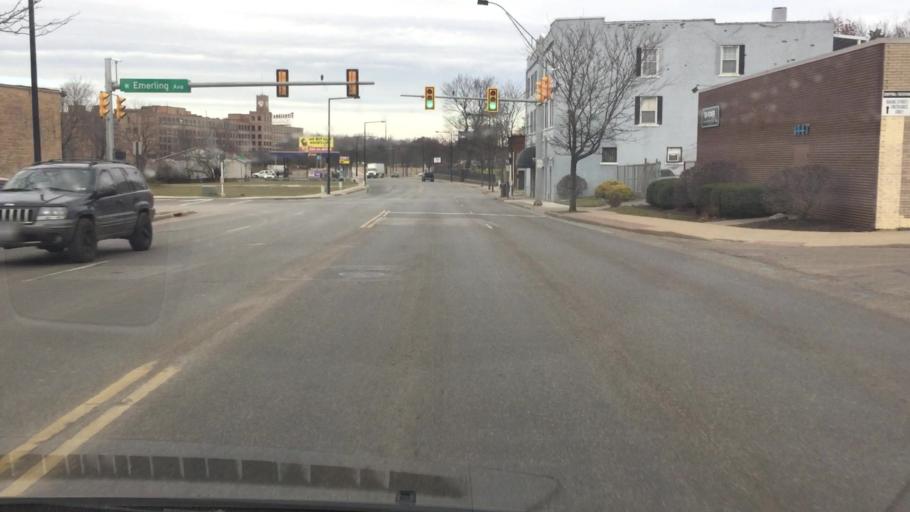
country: US
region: Ohio
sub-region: Summit County
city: Akron
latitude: 41.0473
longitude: -81.5275
